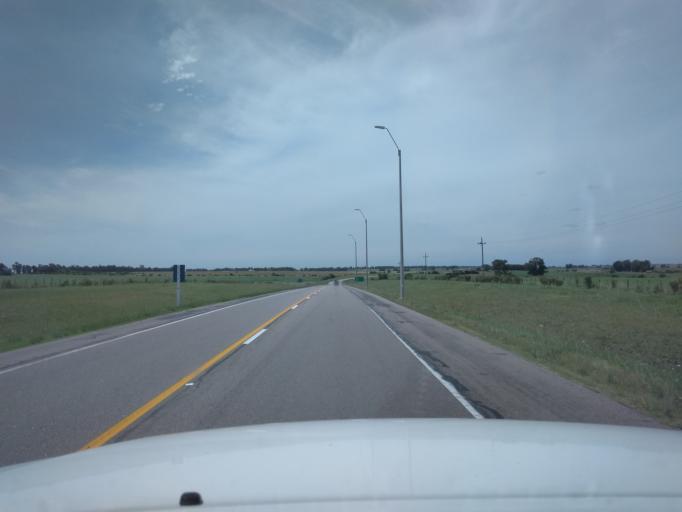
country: UY
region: Florida
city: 25 de Mayo
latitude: -34.2369
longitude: -56.2131
